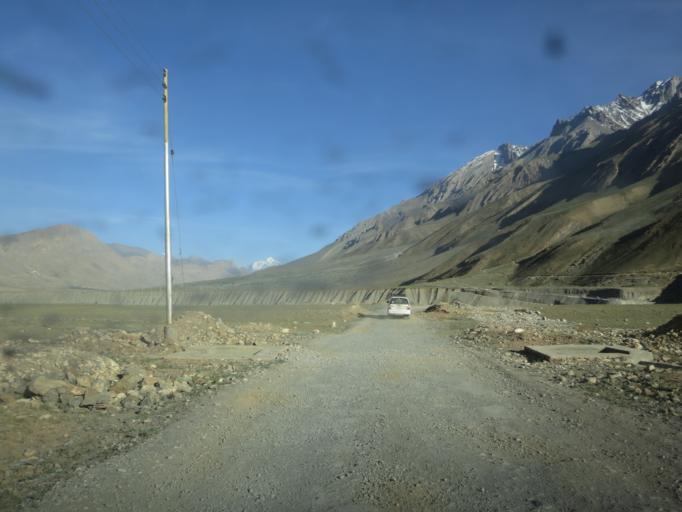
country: IN
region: Himachal Pradesh
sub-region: Kulu
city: Manali
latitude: 32.3310
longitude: 77.9289
